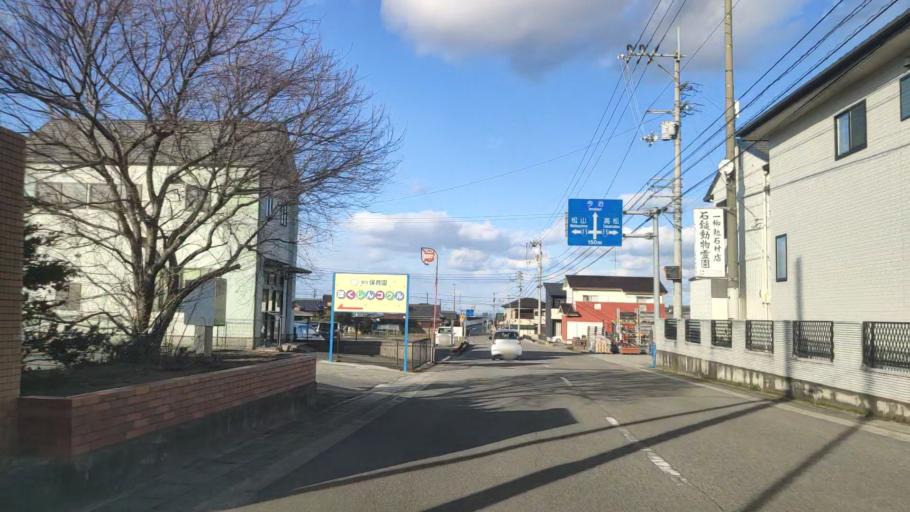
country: JP
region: Ehime
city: Saijo
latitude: 33.8932
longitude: 133.1320
